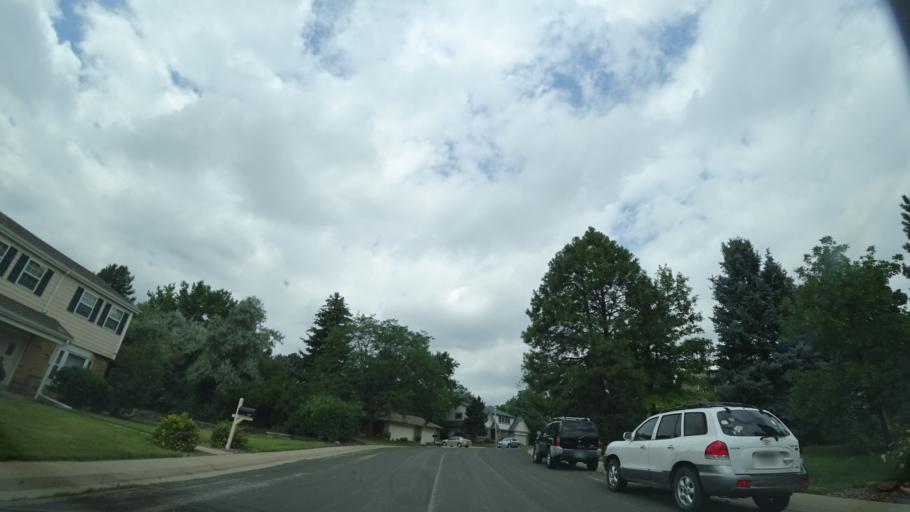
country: US
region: Colorado
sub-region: Jefferson County
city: West Pleasant View
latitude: 39.7127
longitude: -105.1592
